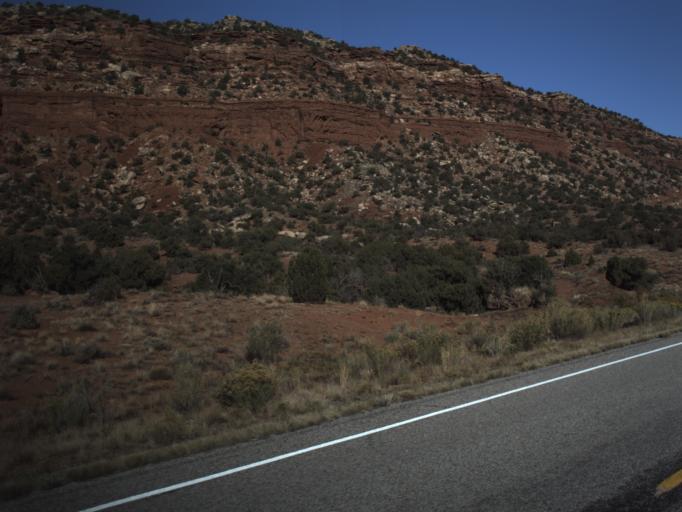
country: US
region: Utah
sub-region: San Juan County
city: Blanding
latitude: 37.6173
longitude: -110.0832
